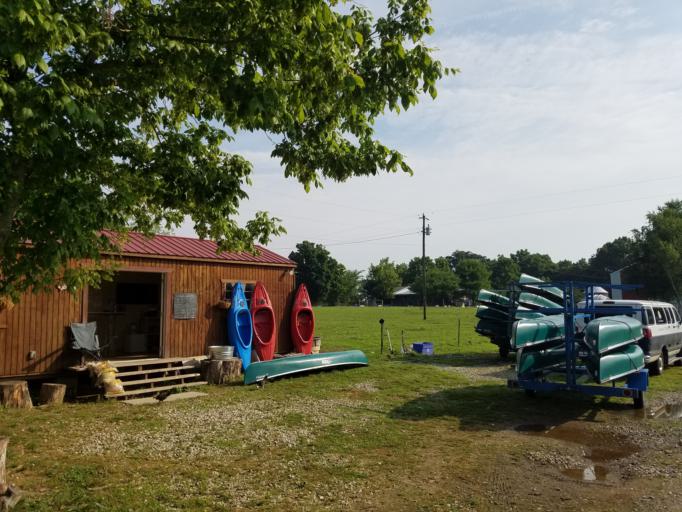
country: US
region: Kentucky
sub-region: Barren County
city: Cave City
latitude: 37.1477
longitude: -86.0402
